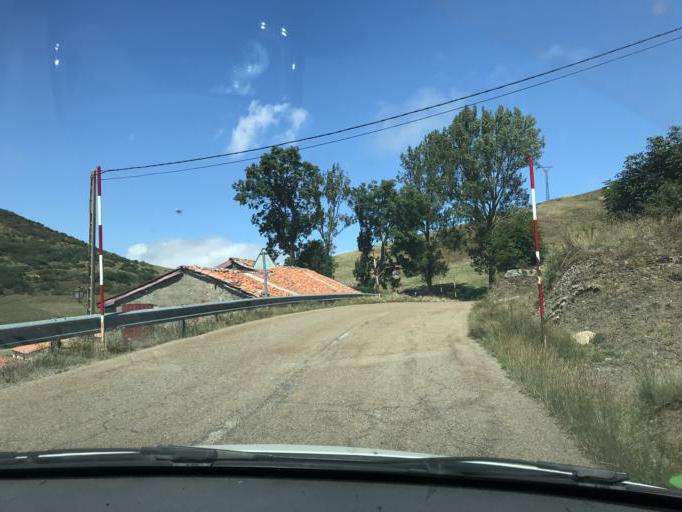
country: ES
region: Castille and Leon
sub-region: Provincia de Palencia
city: Polentinos
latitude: 43.0367
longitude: -4.4571
